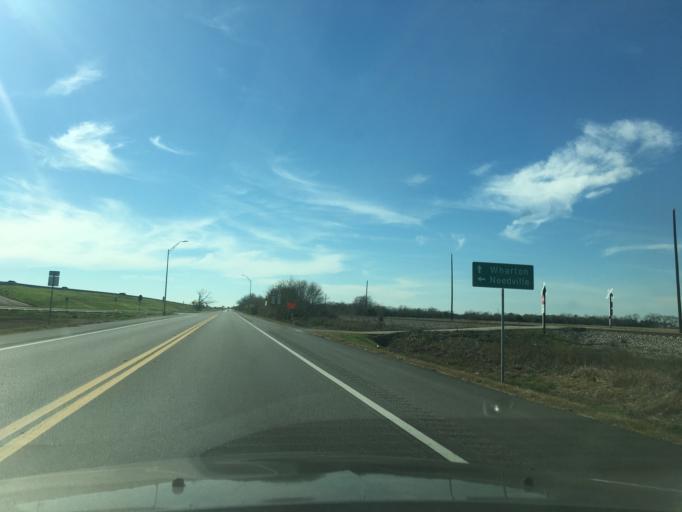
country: US
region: Texas
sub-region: Fort Bend County
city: Pleak
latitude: 29.4861
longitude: -95.9365
